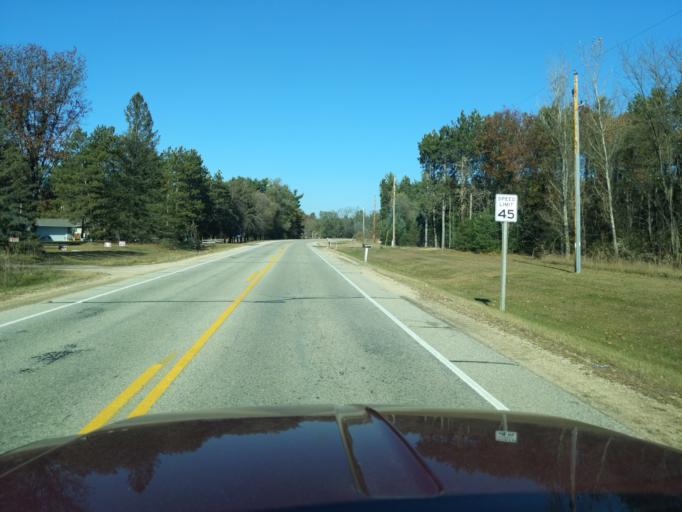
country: US
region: Wisconsin
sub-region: Waushara County
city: Wautoma
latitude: 44.0604
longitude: -89.2959
